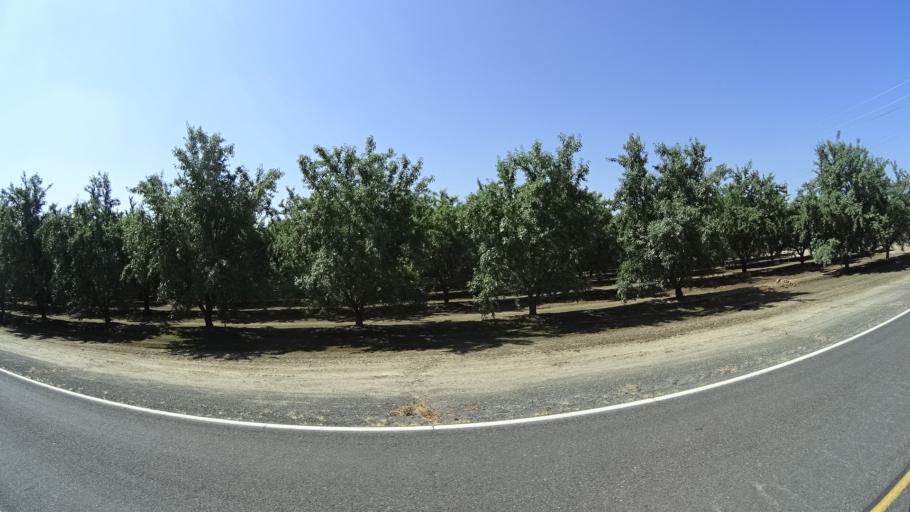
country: US
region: California
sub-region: Fresno County
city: Kingsburg
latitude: 36.4524
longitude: -119.5819
